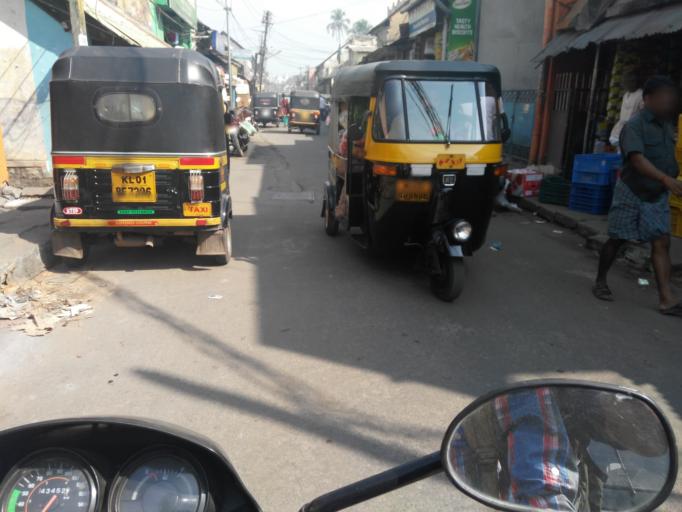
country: IN
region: Kerala
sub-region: Thiruvananthapuram
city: Thiruvananthapuram
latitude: 8.4801
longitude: 76.9505
